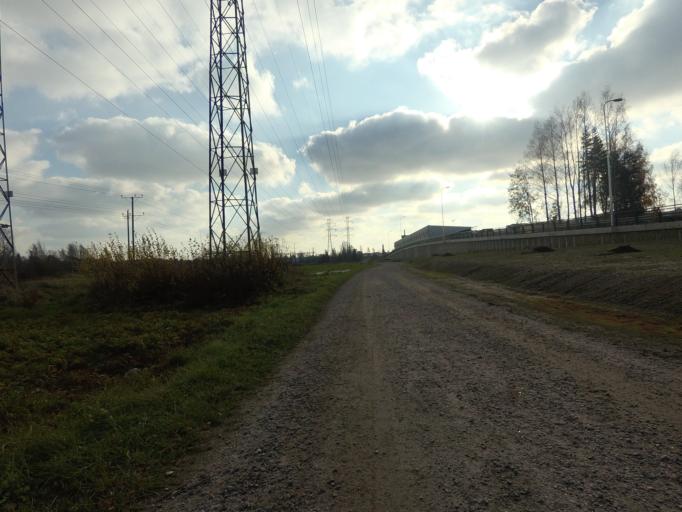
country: FI
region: Uusimaa
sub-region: Helsinki
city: Kauniainen
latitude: 60.1658
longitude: 24.7081
